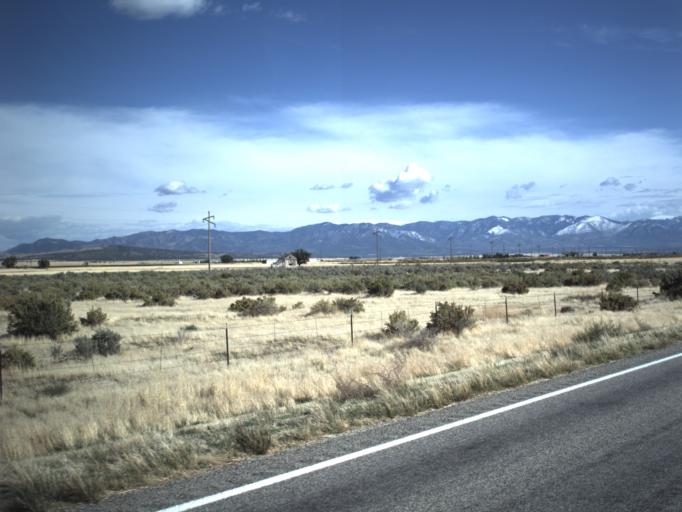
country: US
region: Utah
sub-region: Millard County
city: Delta
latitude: 39.2224
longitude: -112.4218
